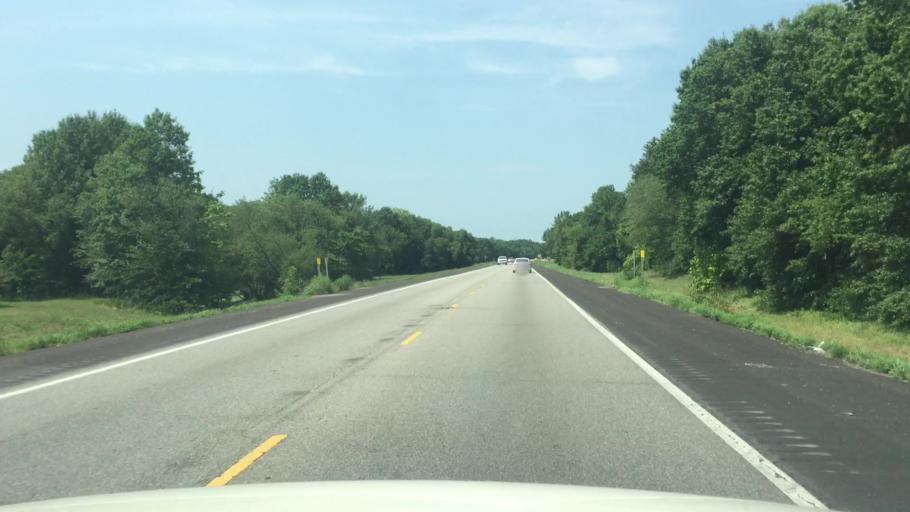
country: US
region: Kansas
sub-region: Crawford County
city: Pittsburg
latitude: 37.4009
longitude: -94.7214
